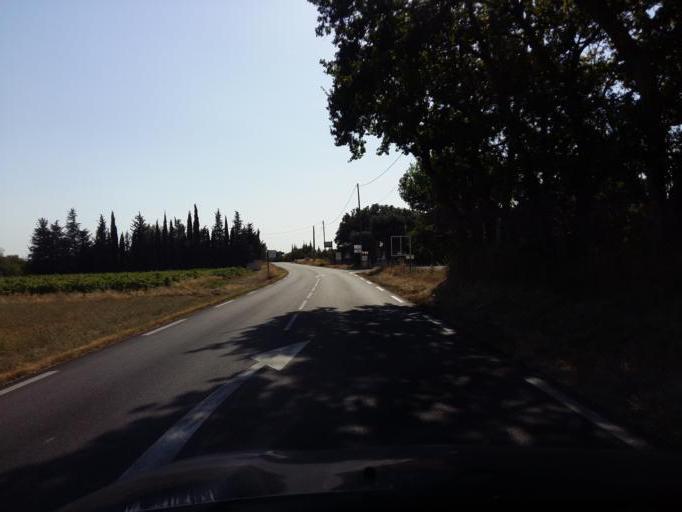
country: FR
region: Provence-Alpes-Cote d'Azur
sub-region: Departement du Vaucluse
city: Saint-Didier
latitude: 44.0197
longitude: 5.0853
